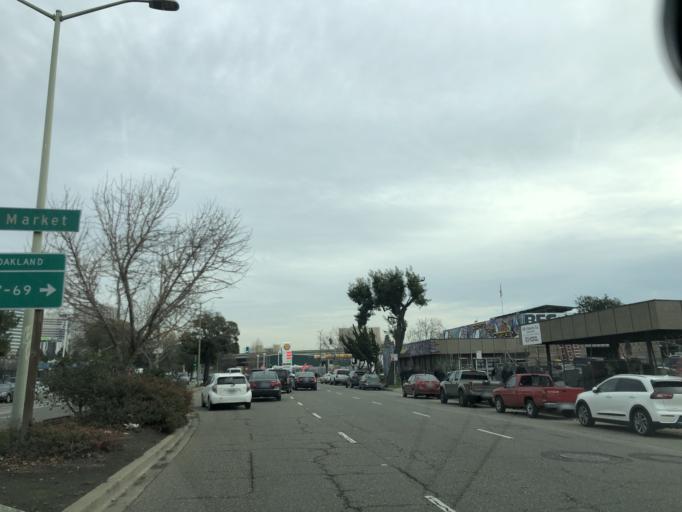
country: US
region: California
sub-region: Alameda County
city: Oakland
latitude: 37.8030
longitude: -122.2842
